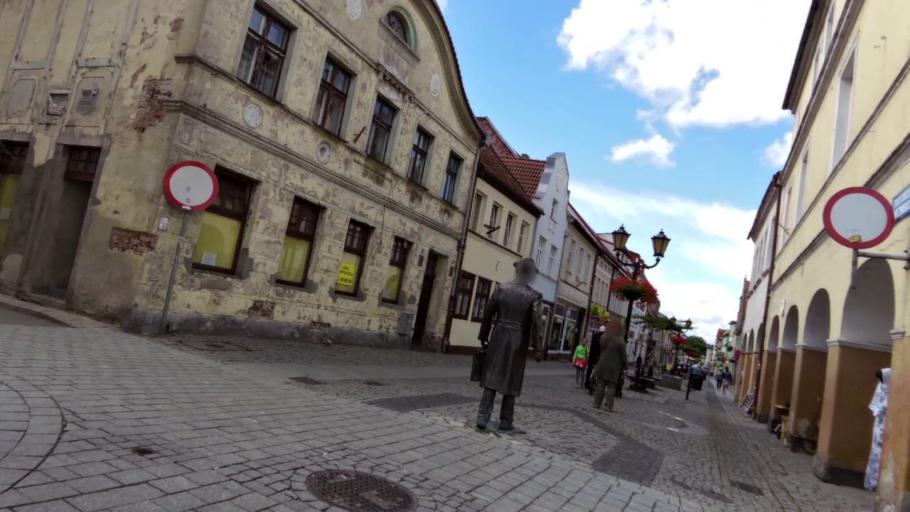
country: PL
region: West Pomeranian Voivodeship
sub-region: Powiat slawienski
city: Darlowo
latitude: 54.4218
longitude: 16.4113
